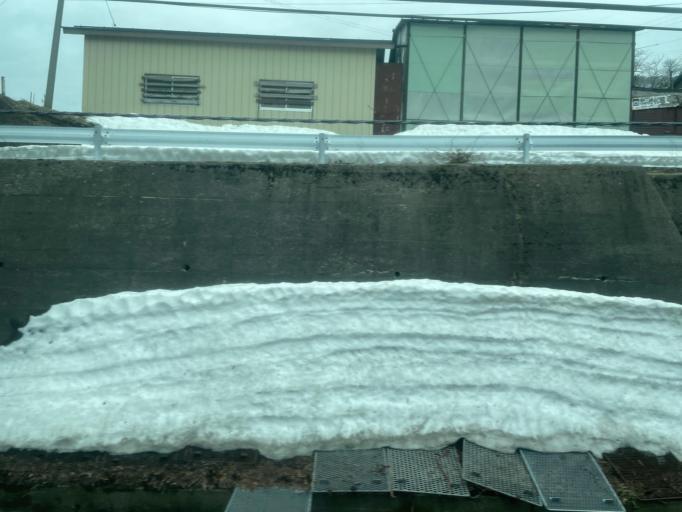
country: JP
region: Gunma
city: Numata
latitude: 36.7976
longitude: 138.9874
